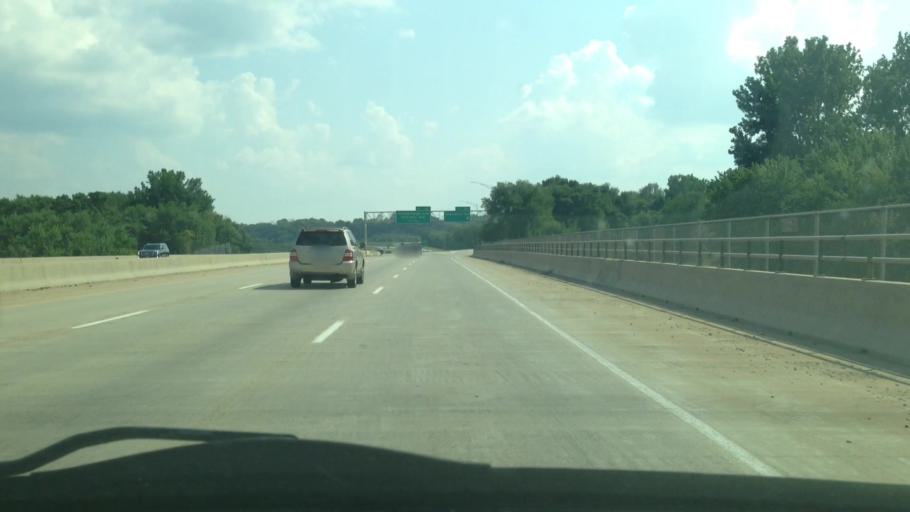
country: US
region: Iowa
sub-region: Black Hawk County
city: Waterloo
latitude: 42.5213
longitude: -92.3899
